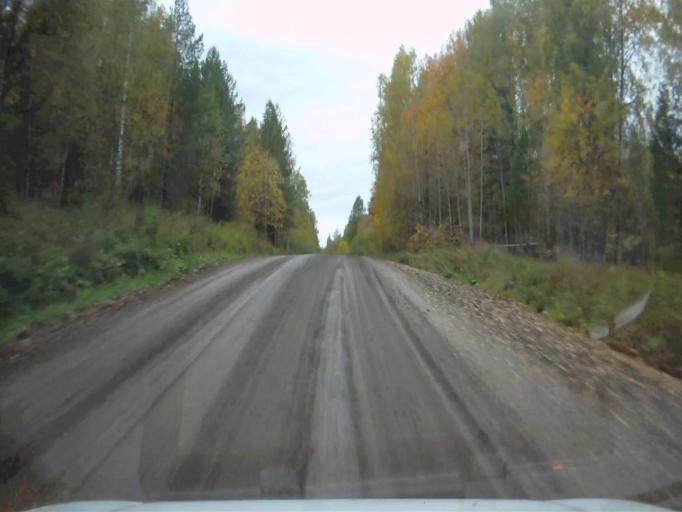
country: RU
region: Chelyabinsk
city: Nyazepetrovsk
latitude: 56.1061
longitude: 59.3827
